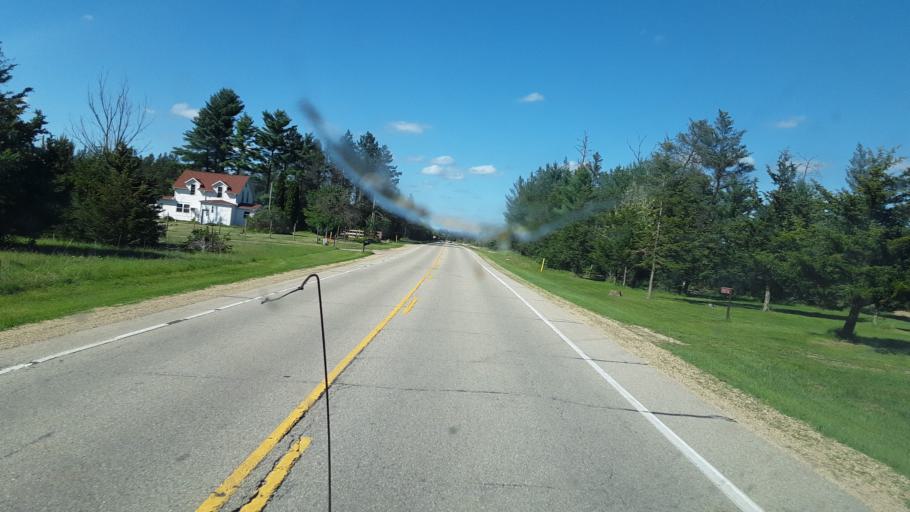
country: US
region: Wisconsin
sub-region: Juneau County
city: New Lisbon
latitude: 43.9381
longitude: -90.0981
